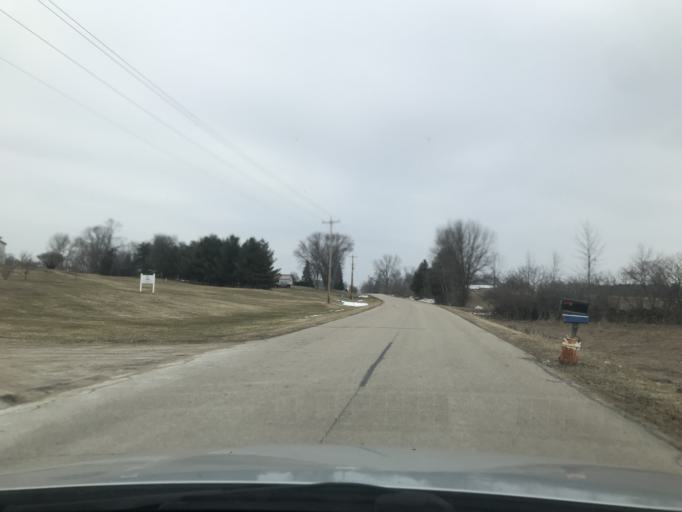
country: US
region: Wisconsin
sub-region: Marinette County
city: Peshtigo
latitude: 45.0385
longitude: -87.8621
